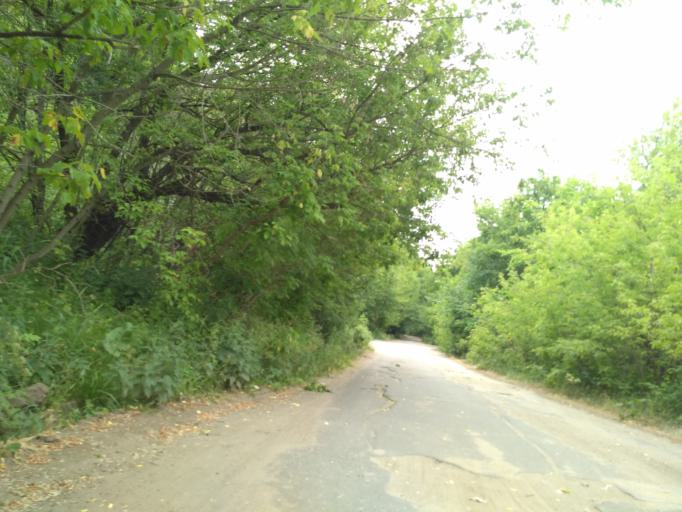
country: RU
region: Nizjnij Novgorod
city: Nizhniy Novgorod
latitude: 56.2925
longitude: 43.9683
